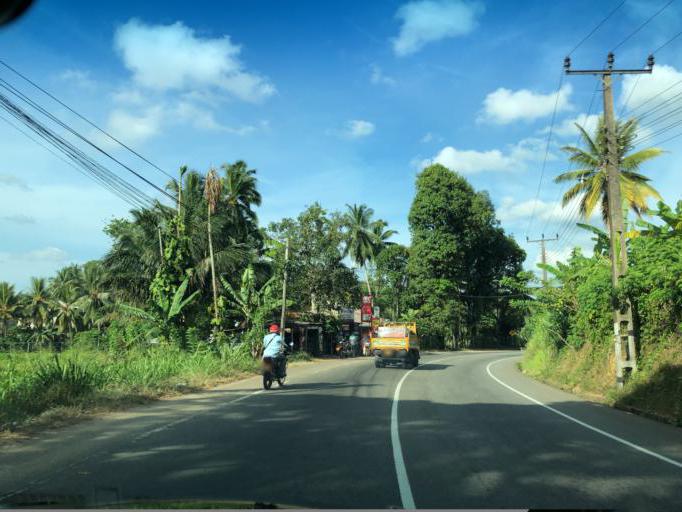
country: LK
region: Western
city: Horawala Junction
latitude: 6.5280
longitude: 80.0938
